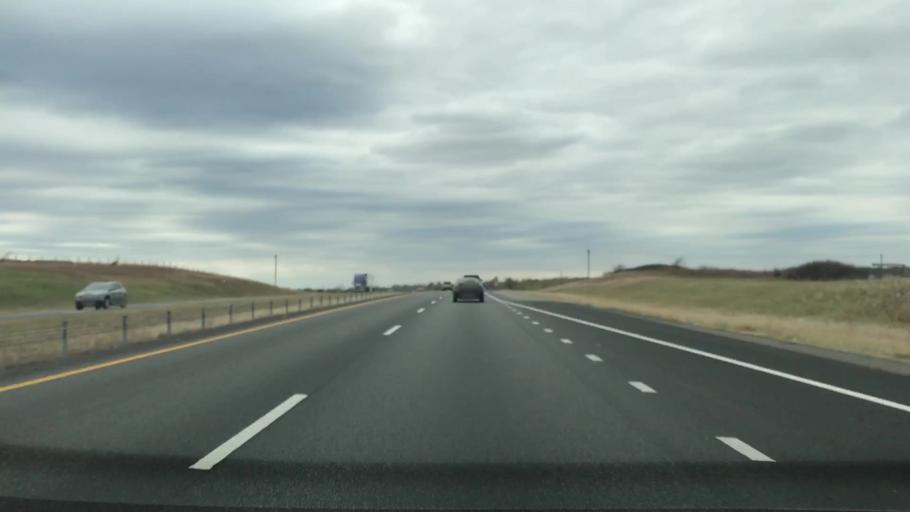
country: US
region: Oklahoma
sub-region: Beckham County
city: Elk City
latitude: 35.3858
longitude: -99.4764
